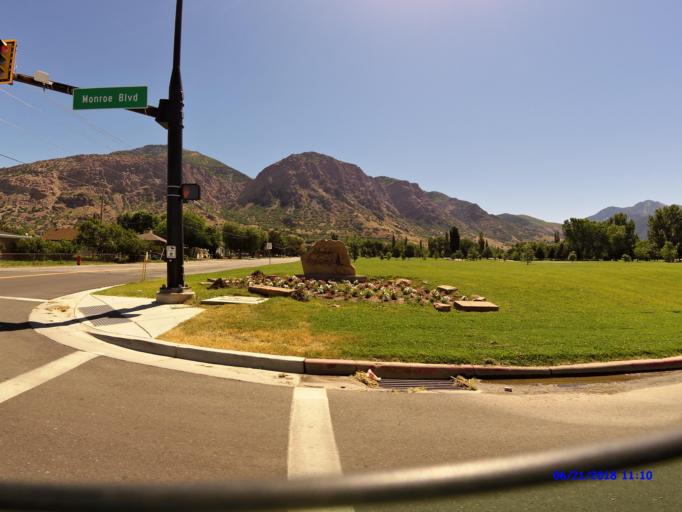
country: US
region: Utah
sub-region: Weber County
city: Harrisville
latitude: 41.2664
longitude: -111.9592
